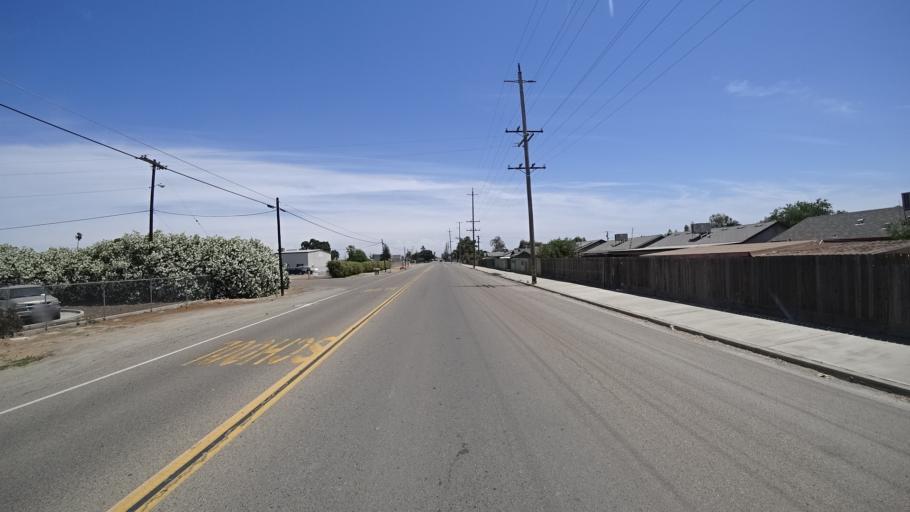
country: US
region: California
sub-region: Kings County
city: Armona
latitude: 36.3135
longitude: -119.7041
